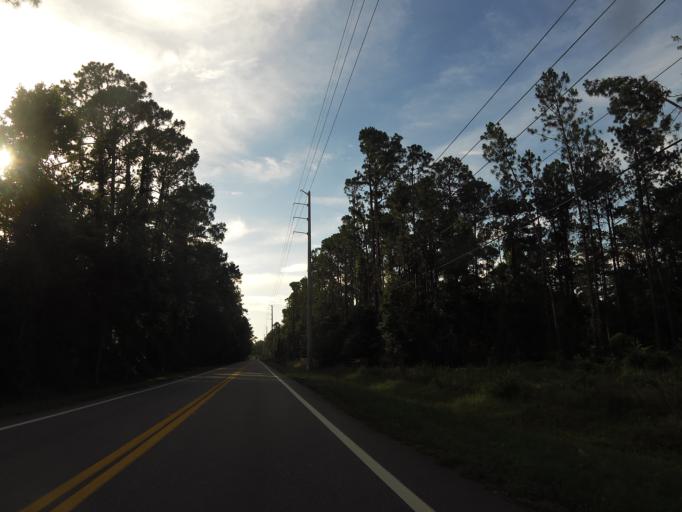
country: US
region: Florida
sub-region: Clay County
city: Green Cove Springs
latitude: 30.0097
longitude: -81.5549
